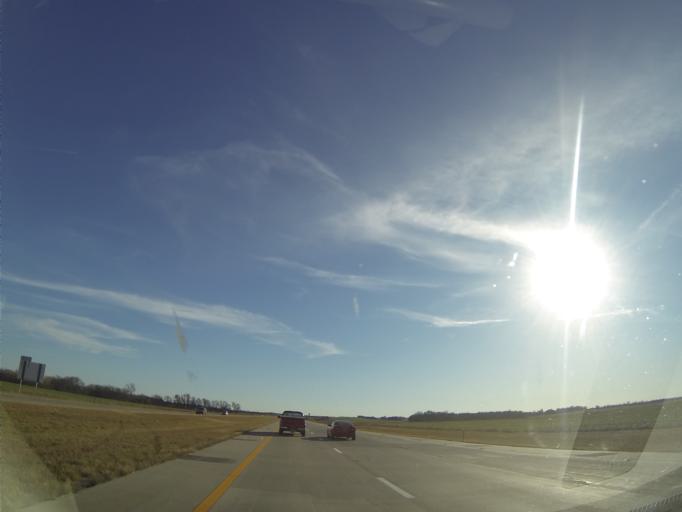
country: US
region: Kansas
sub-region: McPherson County
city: Lindsborg
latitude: 38.6781
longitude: -97.6217
